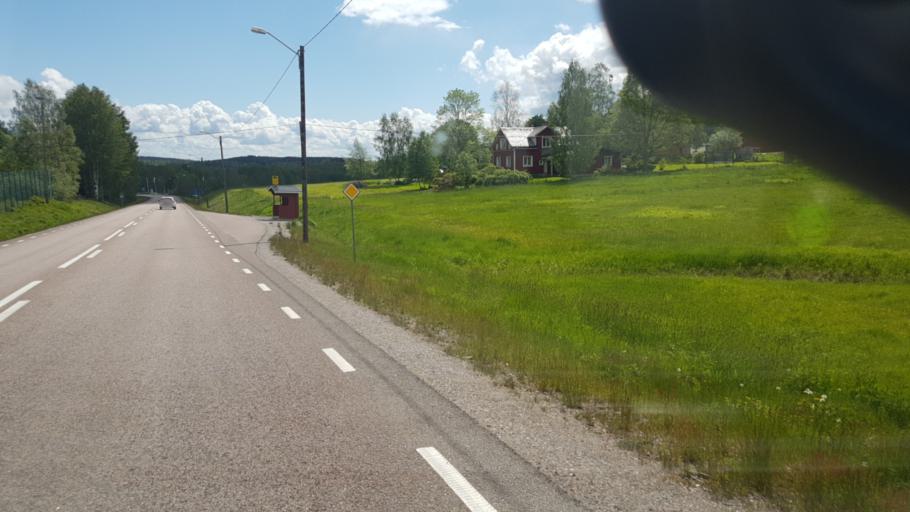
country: SE
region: Vaermland
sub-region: Eda Kommun
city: Amotfors
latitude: 59.6789
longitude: 12.4094
